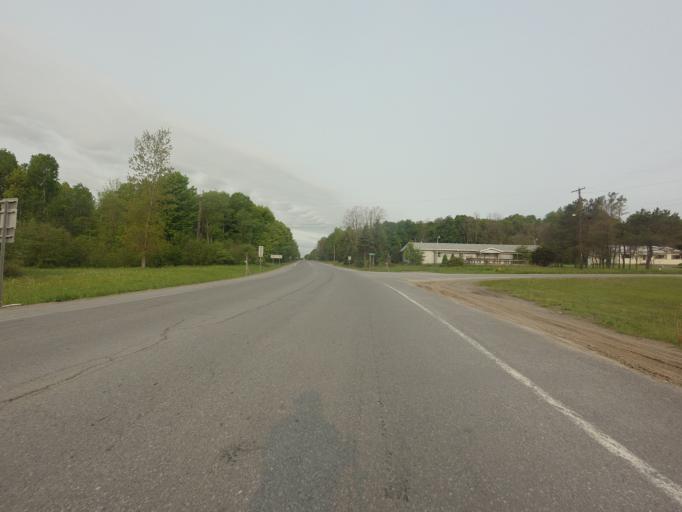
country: US
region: New York
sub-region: Jefferson County
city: Carthage
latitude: 44.0339
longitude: -75.5815
